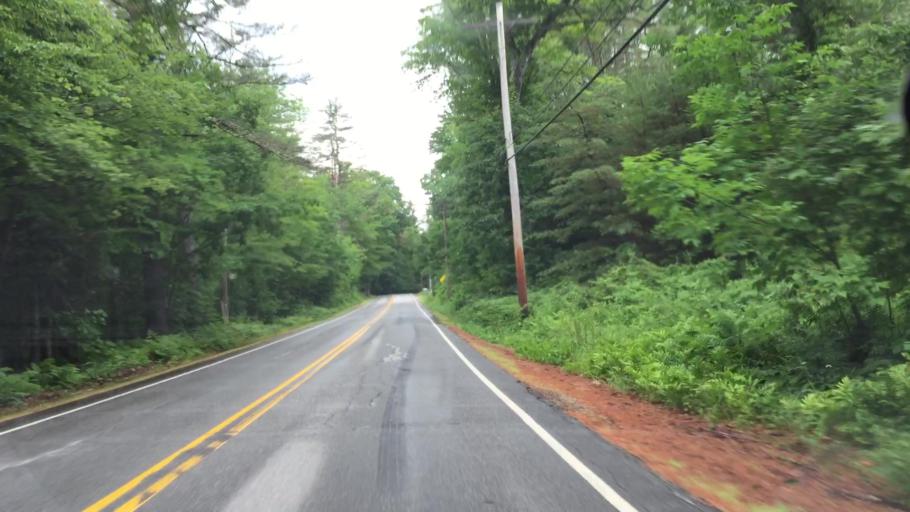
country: US
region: New Hampshire
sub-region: Carroll County
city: Center Harbor
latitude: 43.7297
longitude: -71.4758
